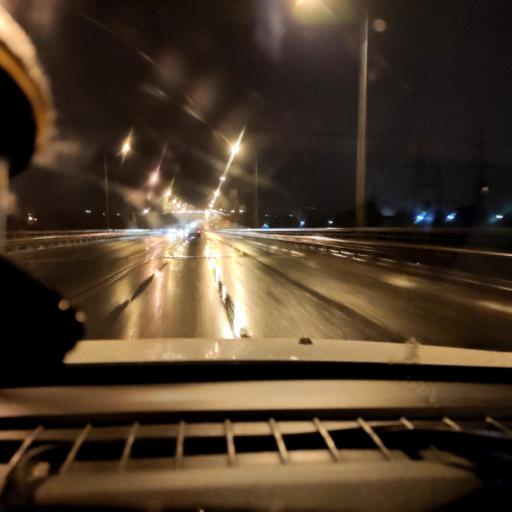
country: RU
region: Samara
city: Samara
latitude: 53.1690
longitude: 50.1958
